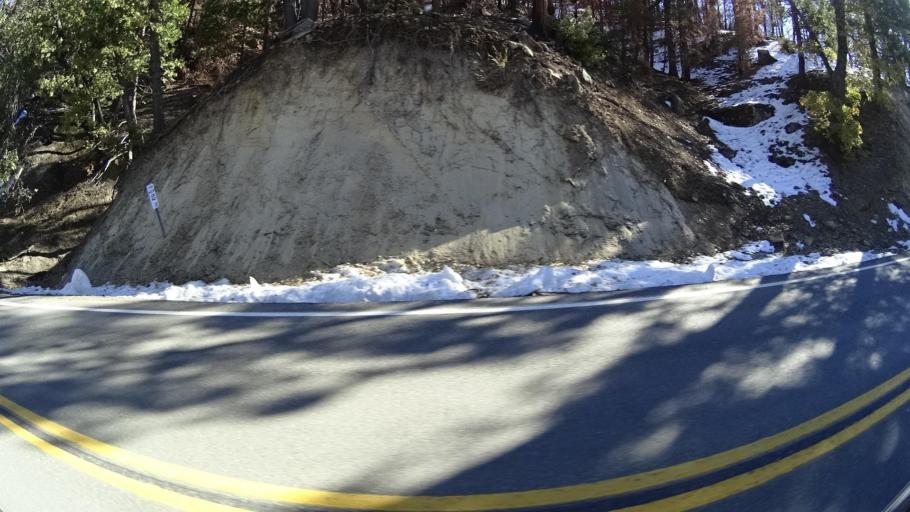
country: US
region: California
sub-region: Kern County
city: Alta Sierra
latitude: 35.7502
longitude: -118.5583
